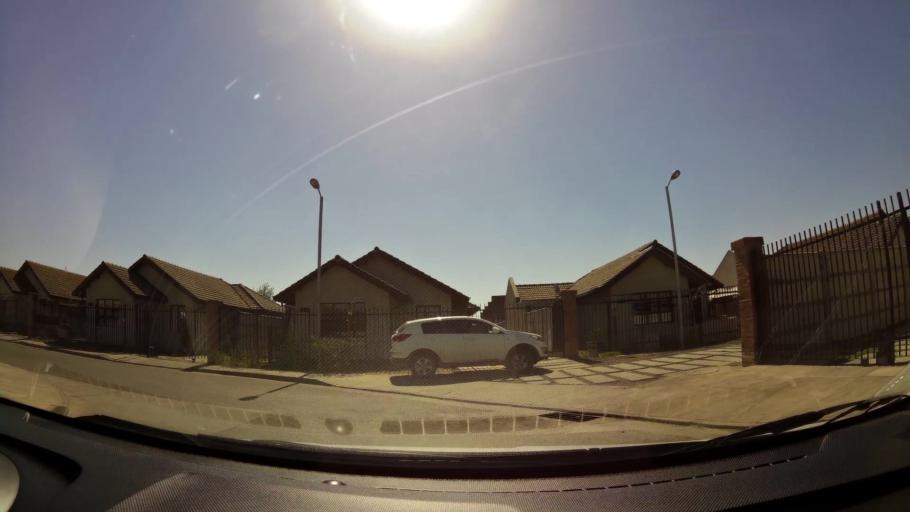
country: CL
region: Maule
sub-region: Provincia de Talca
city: Talca
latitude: -35.4287
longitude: -71.6129
